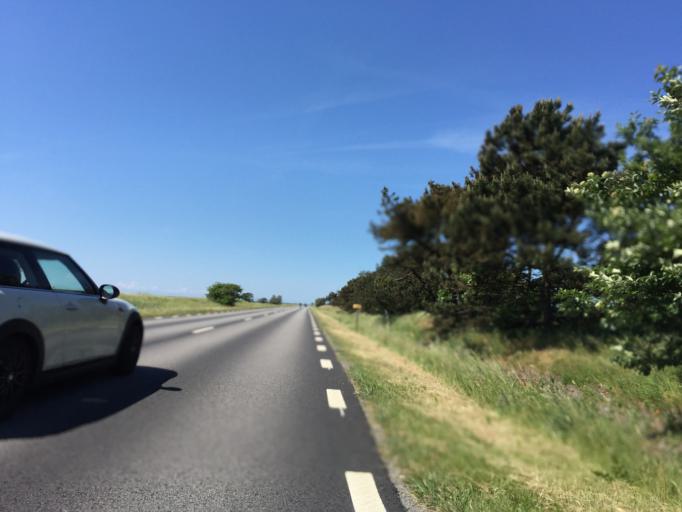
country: SE
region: Skane
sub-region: Trelleborgs Kommun
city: Skare
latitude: 55.3786
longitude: 13.0461
